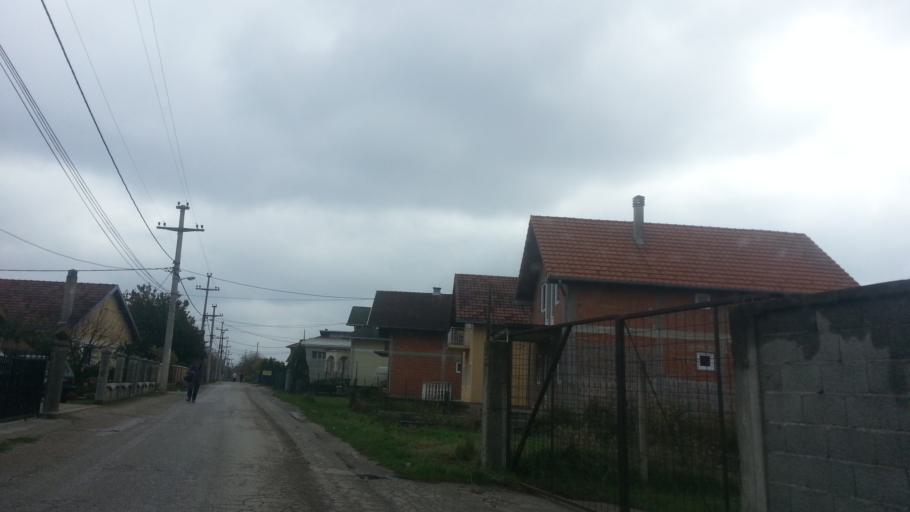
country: RS
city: Novi Banovci
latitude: 44.9169
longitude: 20.2808
